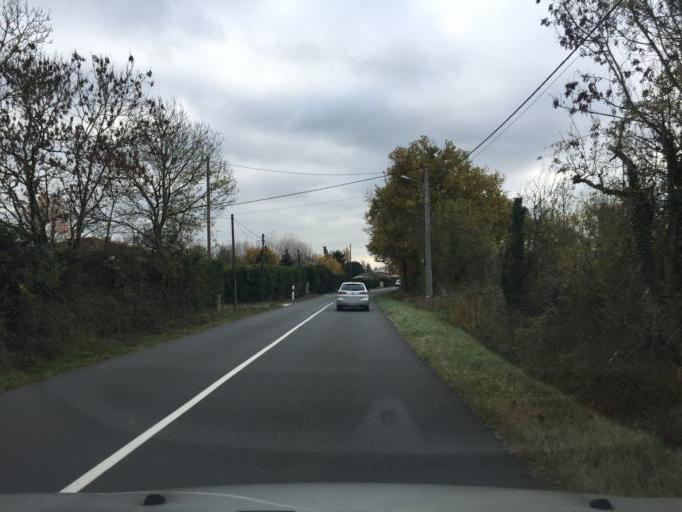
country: FR
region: Rhone-Alpes
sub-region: Departement de l'Ain
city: Saint-Didier-de-Formans
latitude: 45.9518
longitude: 4.8065
